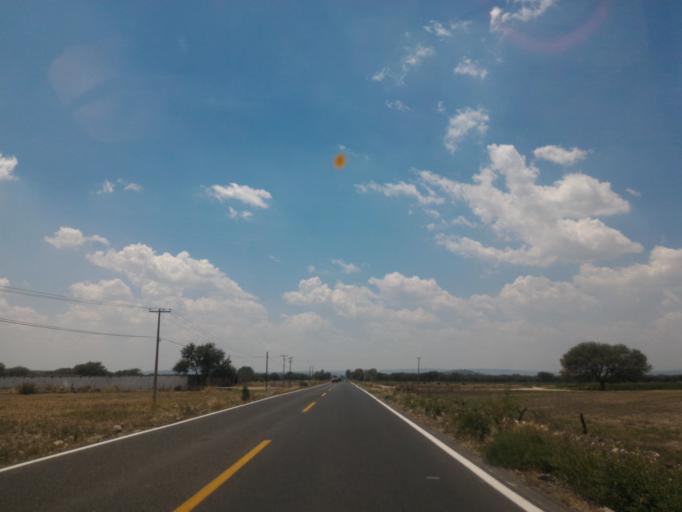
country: MX
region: Guanajuato
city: Ciudad Manuel Doblado
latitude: 20.7644
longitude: -101.9696
